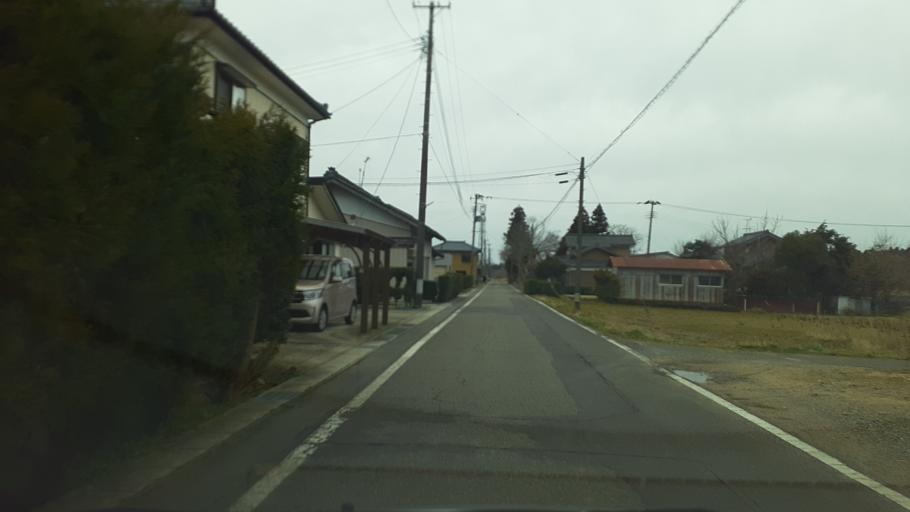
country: JP
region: Niigata
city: Gosen
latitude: 37.7394
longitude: 139.2606
